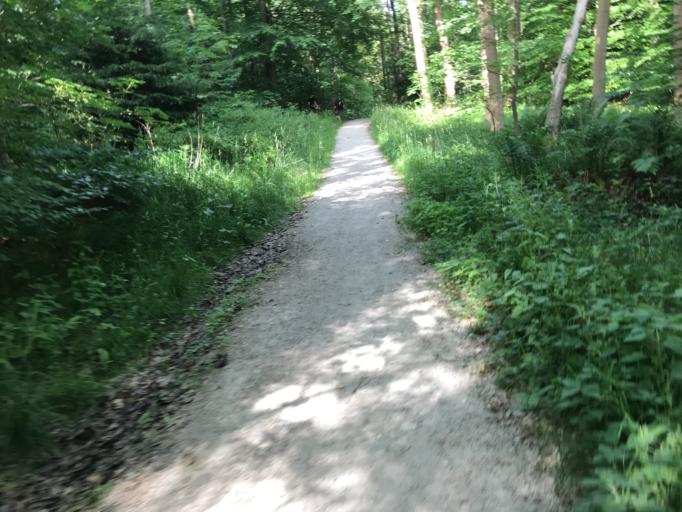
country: DK
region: Capital Region
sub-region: Ballerup Kommune
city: Ballerup
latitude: 55.7572
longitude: 12.3602
